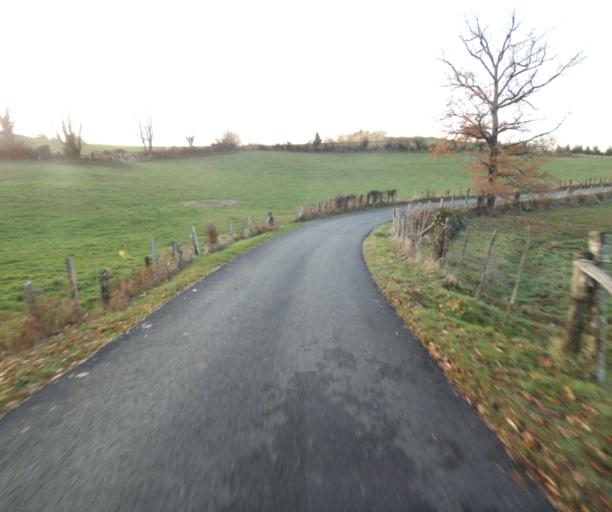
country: FR
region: Limousin
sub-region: Departement de la Correze
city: Laguenne
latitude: 45.2329
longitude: 1.8222
